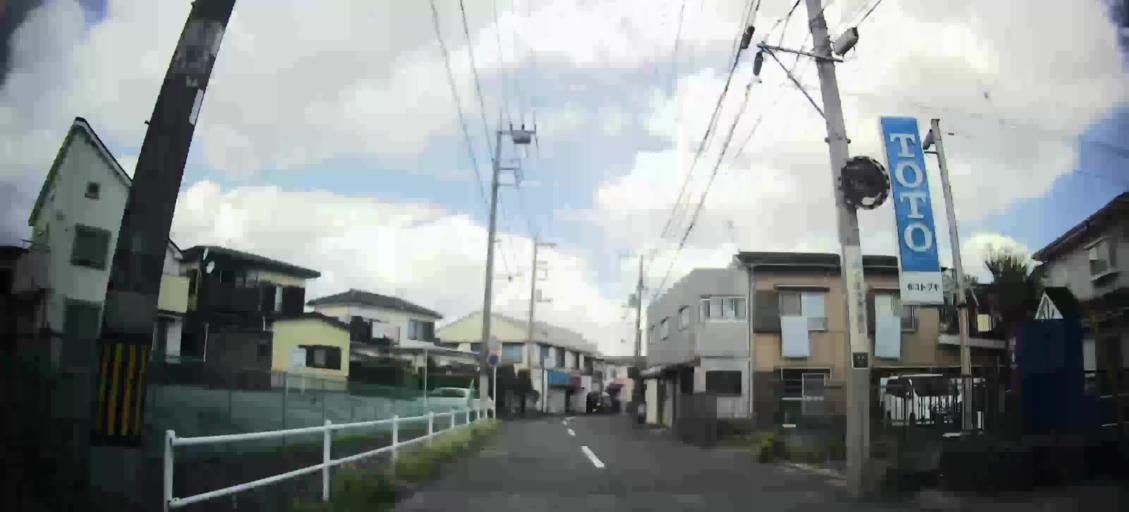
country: JP
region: Kanagawa
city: Yokohama
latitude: 35.4670
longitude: 139.5607
